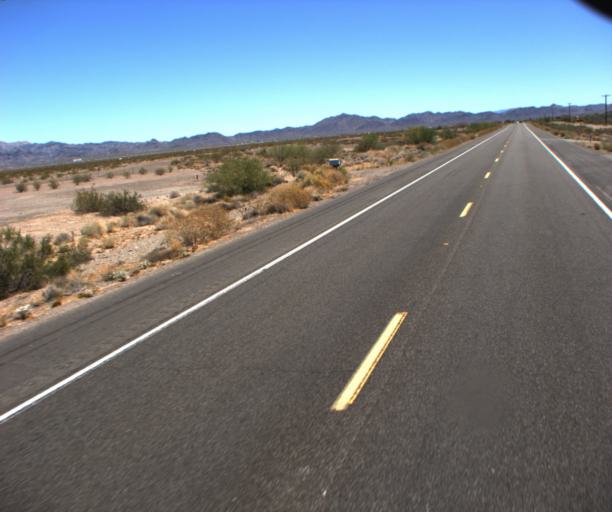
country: US
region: Arizona
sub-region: La Paz County
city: Salome
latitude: 33.7131
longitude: -113.7969
